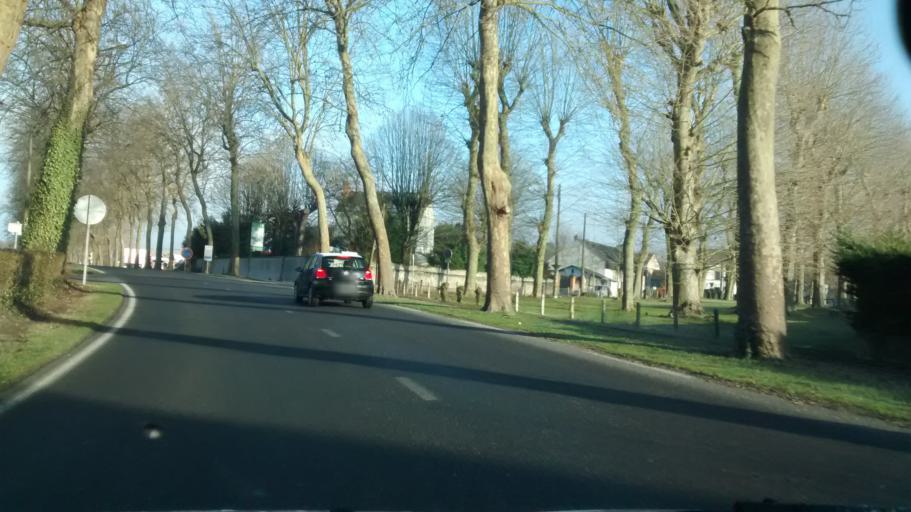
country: FR
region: Centre
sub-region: Departement d'Indre-et-Loire
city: Montbazon
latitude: 47.2908
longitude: 0.7189
